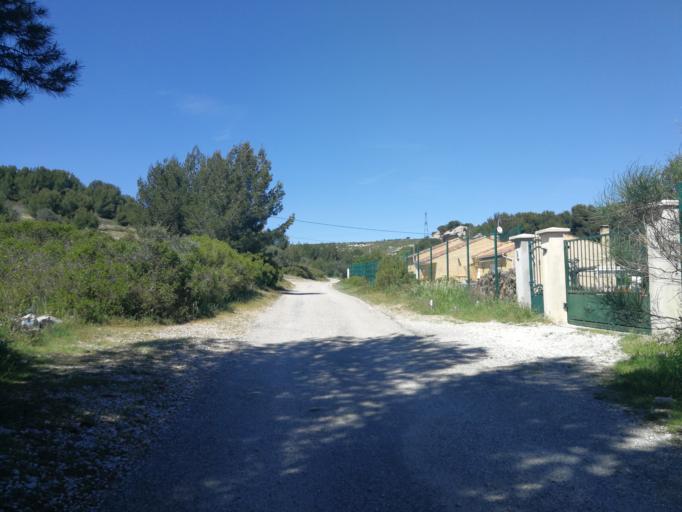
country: FR
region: Provence-Alpes-Cote d'Azur
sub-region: Departement des Bouches-du-Rhone
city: Sausset-les-Pins
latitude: 43.3422
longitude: 5.0484
